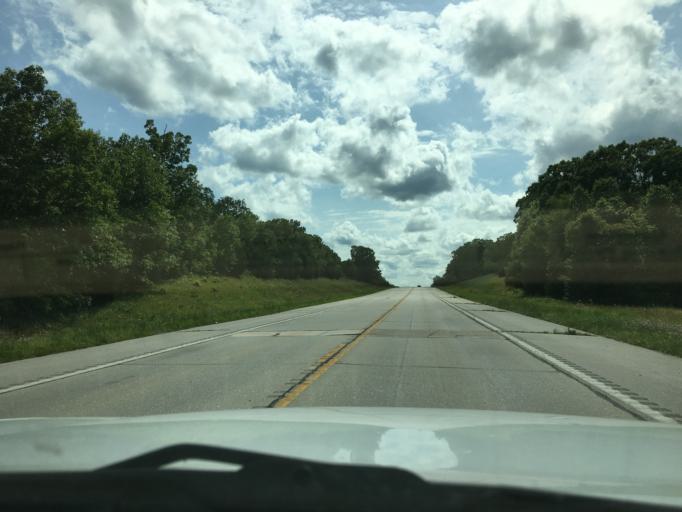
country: US
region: Missouri
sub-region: Franklin County
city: Gerald
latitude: 38.4199
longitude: -91.2886
